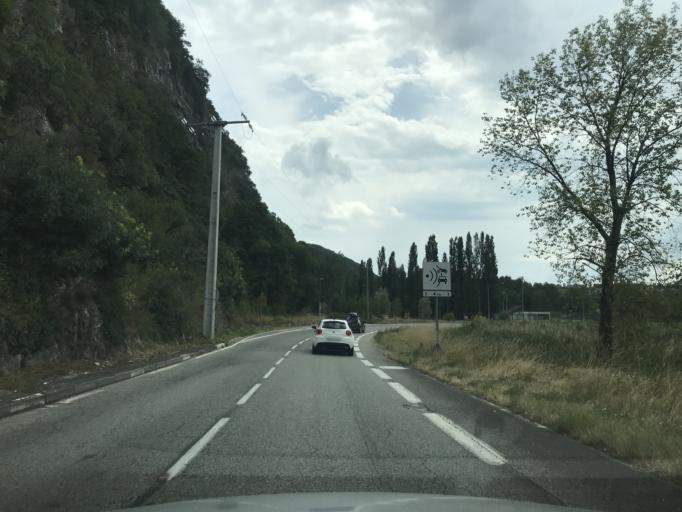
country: FR
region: Rhone-Alpes
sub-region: Departement de la Savoie
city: Brison-Saint-Innocent
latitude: 45.7370
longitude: 5.8929
